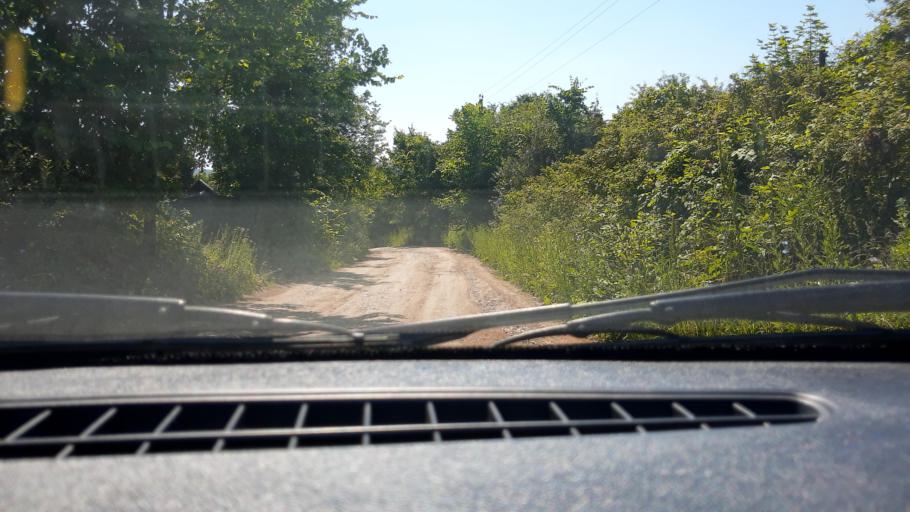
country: RU
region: Bashkortostan
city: Karmaskaly
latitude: 54.3619
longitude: 55.8942
